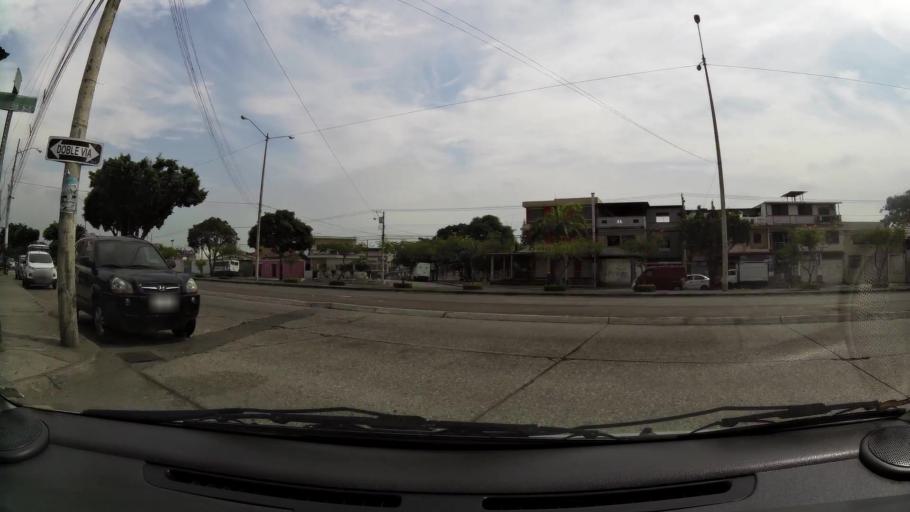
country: EC
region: Guayas
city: Eloy Alfaro
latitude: -2.1234
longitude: -79.9001
